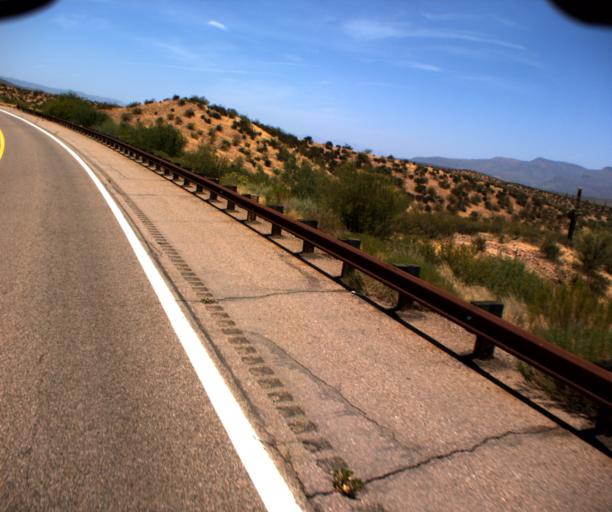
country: US
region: Arizona
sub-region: Gila County
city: Tonto Basin
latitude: 33.6354
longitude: -111.0699
